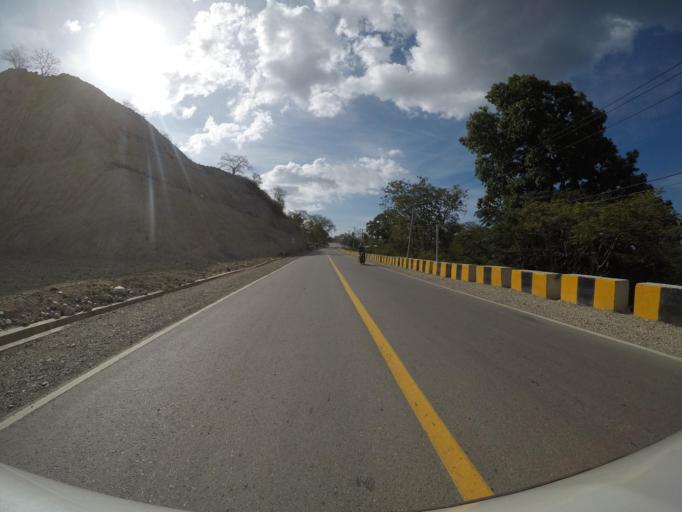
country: TL
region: Baucau
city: Baucau
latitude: -8.4603
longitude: 126.4787
